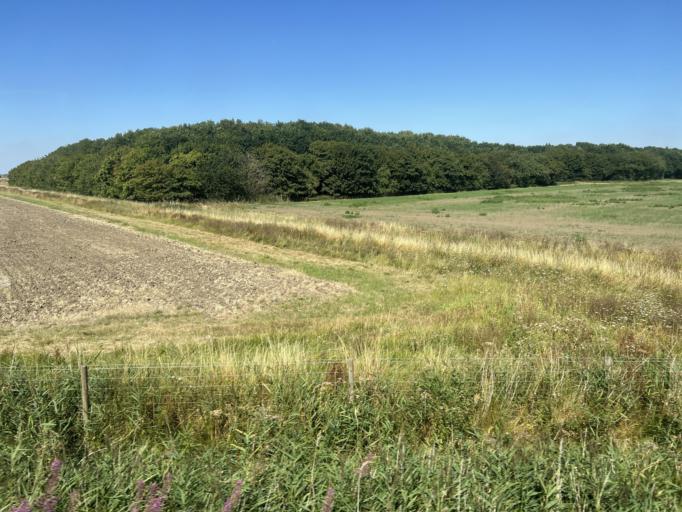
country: GB
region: England
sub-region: Lincolnshire
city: Spilsby
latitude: 53.1132
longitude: 0.1272
